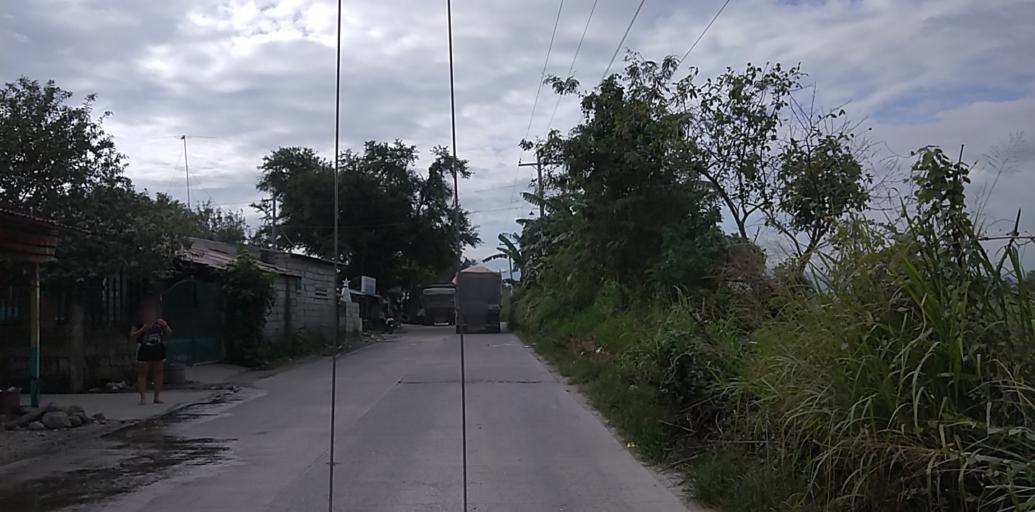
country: PH
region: Central Luzon
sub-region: Province of Pampanga
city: Porac
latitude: 15.0688
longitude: 120.5554
